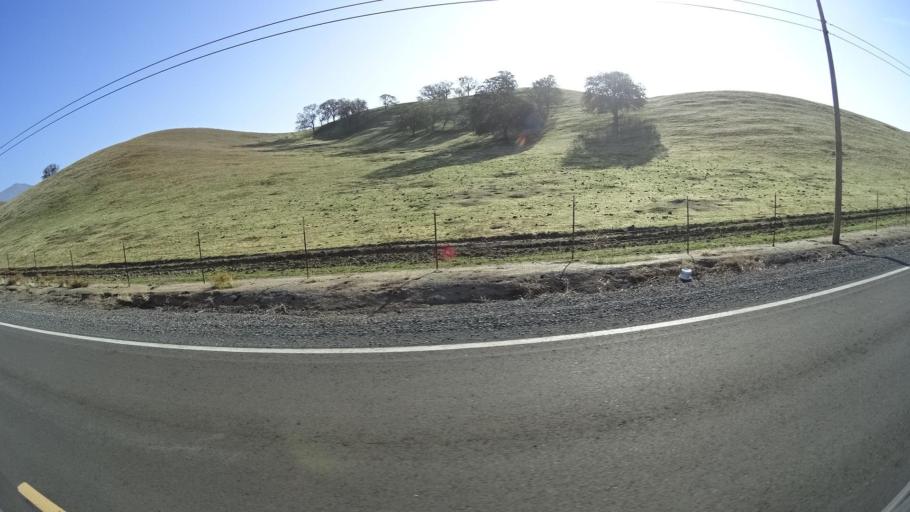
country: US
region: California
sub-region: Tulare County
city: Richgrove
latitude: 35.7190
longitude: -118.8600
